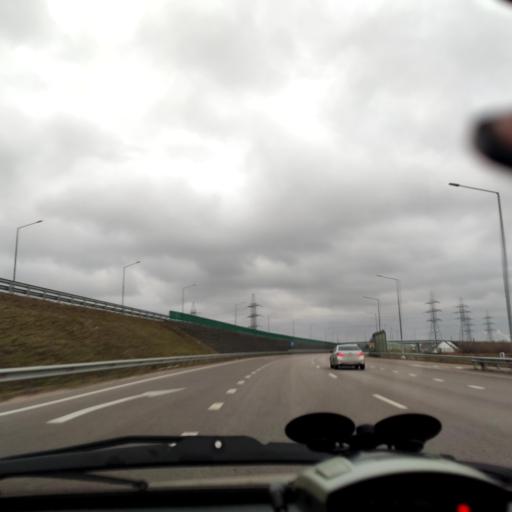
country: RU
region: Voronezj
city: Novaya Usman'
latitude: 51.6420
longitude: 39.3163
